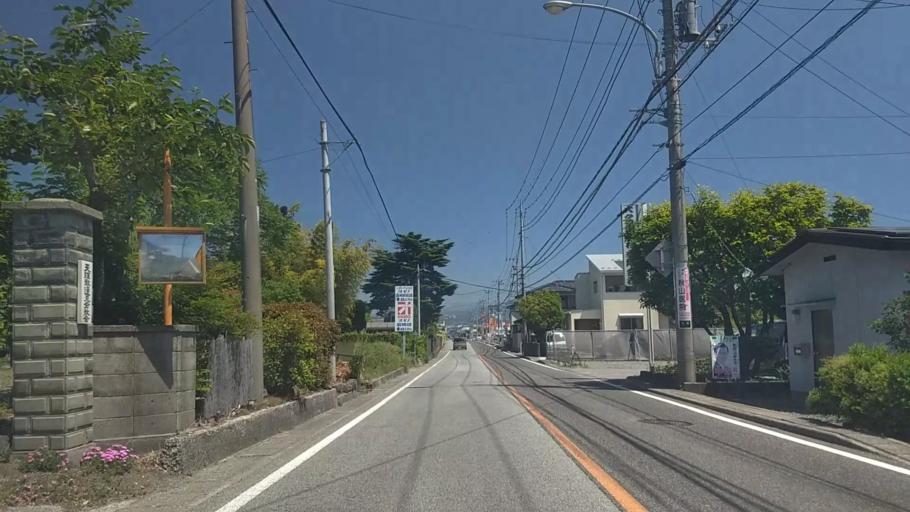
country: JP
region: Yamanashi
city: Nirasaki
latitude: 35.6655
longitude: 138.4645
